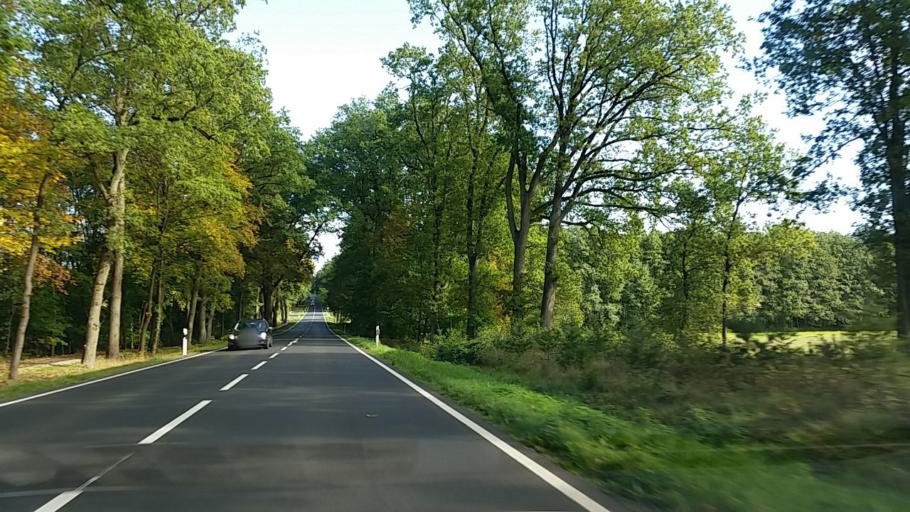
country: DE
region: Lower Saxony
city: Neuenkirchen
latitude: 53.0297
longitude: 9.7179
